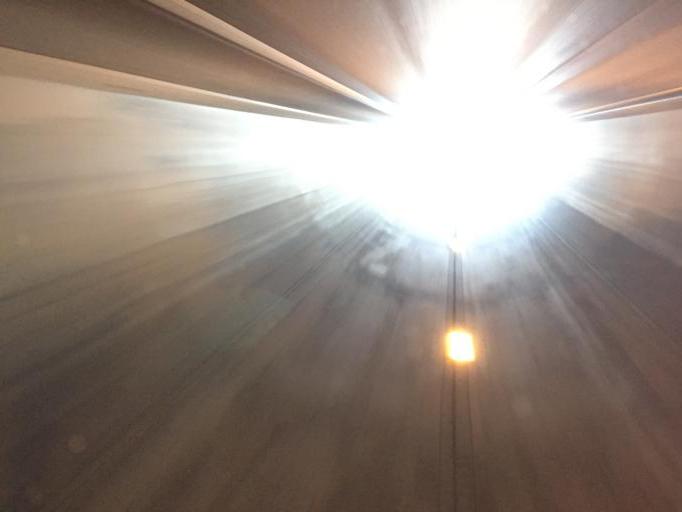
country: NO
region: Akershus
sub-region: Oppegard
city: Kolbotn
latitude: 59.7896
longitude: 10.8396
